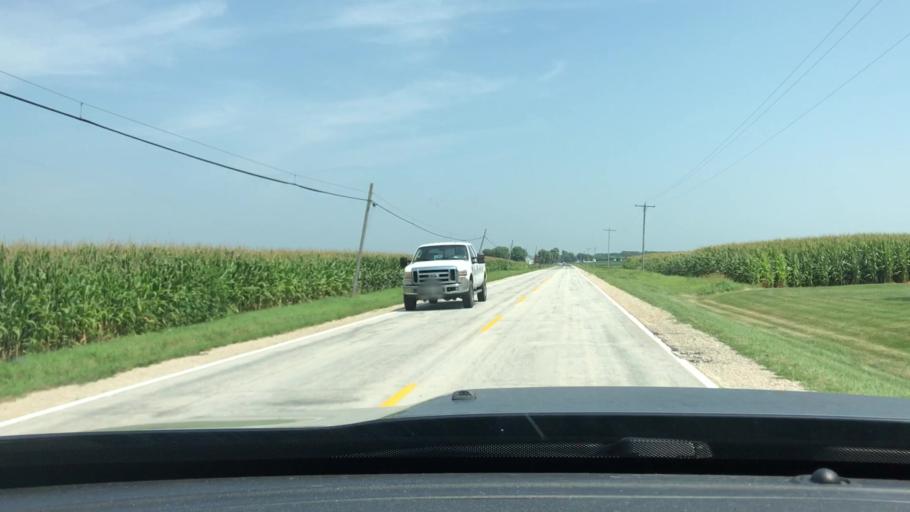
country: US
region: Illinois
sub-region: LaSalle County
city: Sheridan
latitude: 41.5045
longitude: -88.7301
